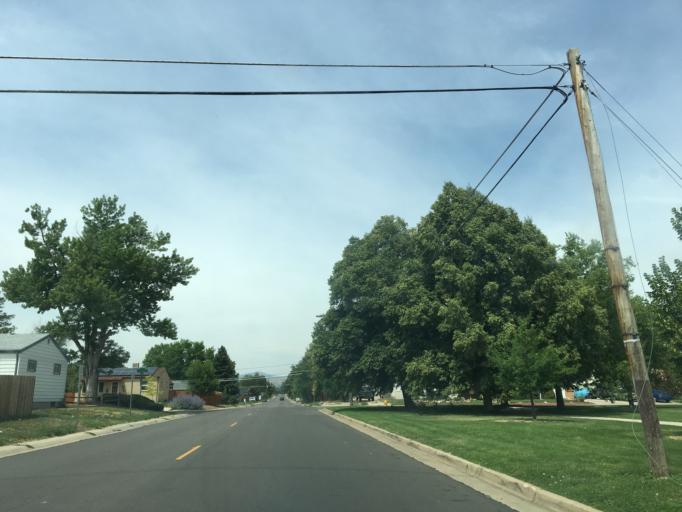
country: US
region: Colorado
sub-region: Jefferson County
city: Lakewood
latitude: 39.6931
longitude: -105.0359
